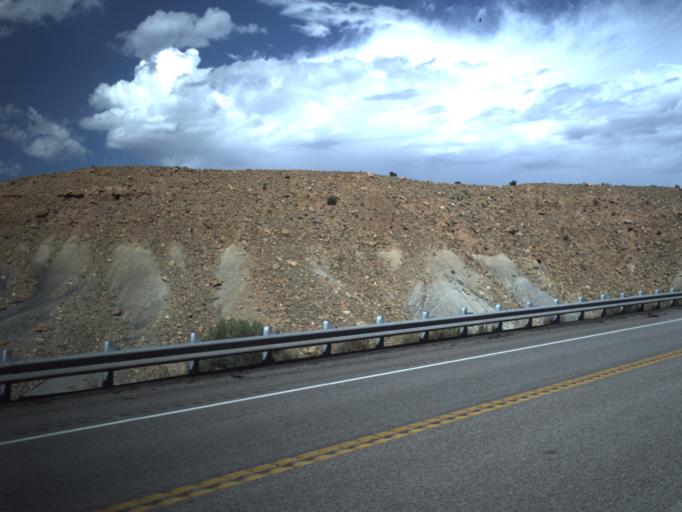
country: US
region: Utah
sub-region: Carbon County
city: East Carbon City
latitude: 39.3941
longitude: -110.4176
